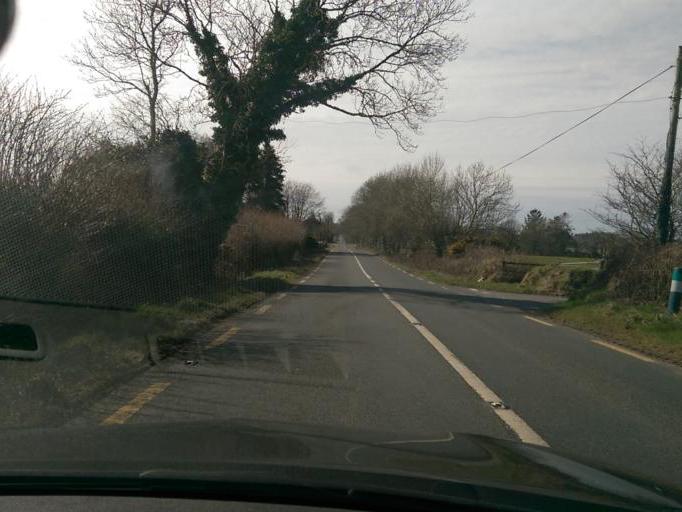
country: IE
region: Connaught
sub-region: County Galway
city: Athenry
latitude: 53.4769
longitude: -8.6170
